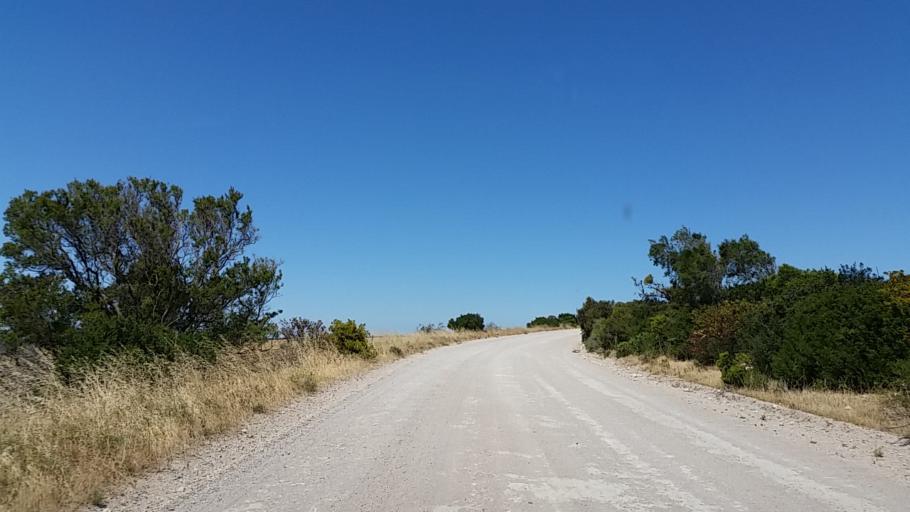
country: AU
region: South Australia
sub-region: Yorke Peninsula
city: Honiton
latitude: -35.0913
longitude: 137.4517
